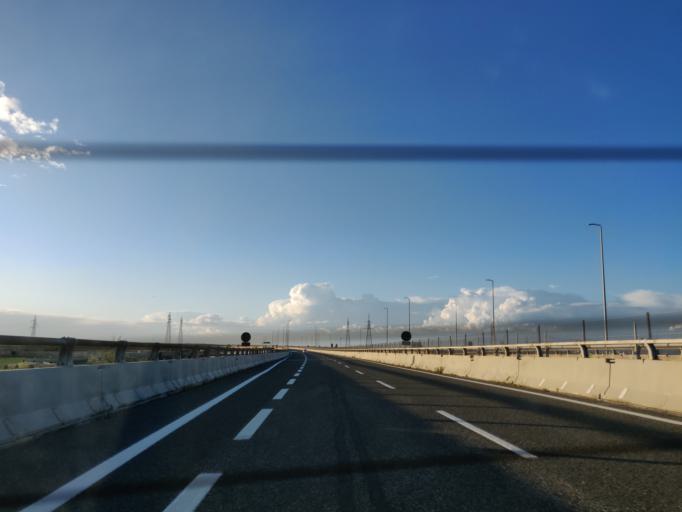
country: IT
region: Tuscany
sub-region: Provincia di Livorno
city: Vicarello
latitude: 43.6106
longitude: 10.4425
